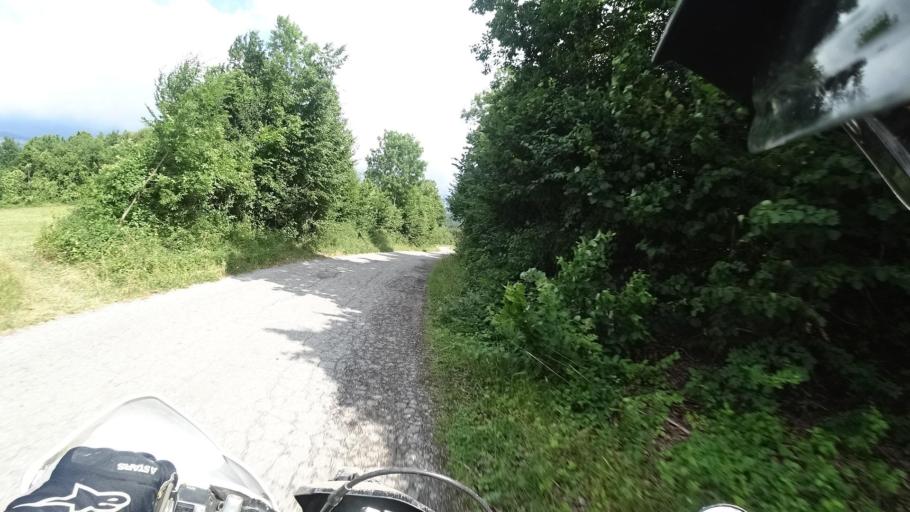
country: HR
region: Zadarska
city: Gracac
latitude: 44.5308
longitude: 15.7757
